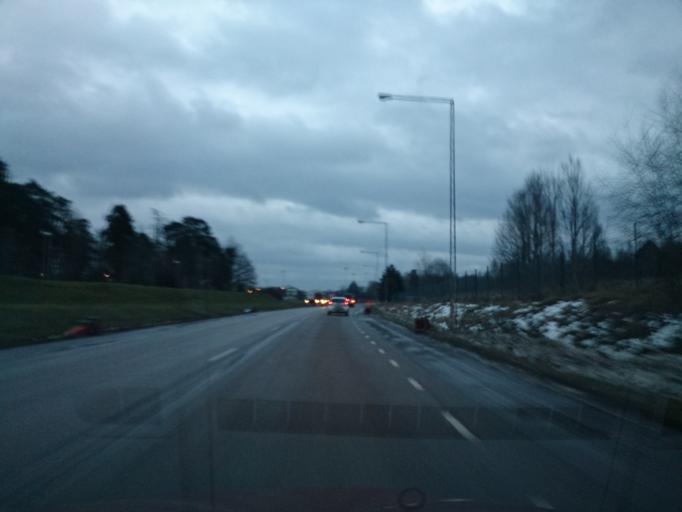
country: SE
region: OEstergoetland
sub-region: Linkopings Kommun
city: Linkoping
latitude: 58.3928
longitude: 15.6160
